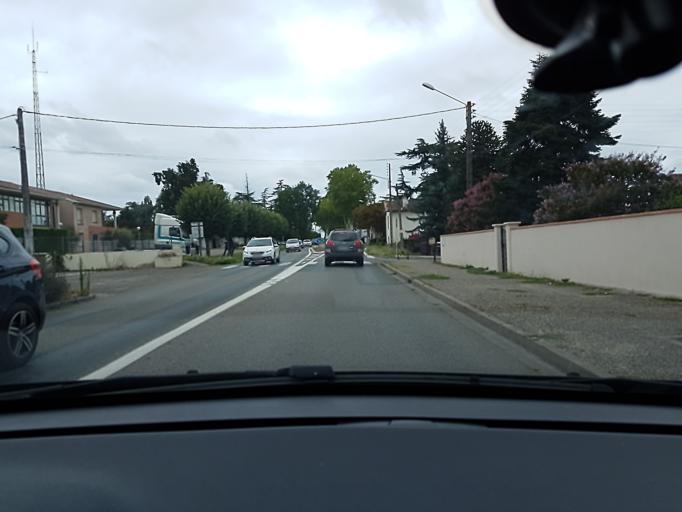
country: FR
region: Aquitaine
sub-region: Departement du Lot-et-Garonne
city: Nerac
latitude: 44.1427
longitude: 0.3322
